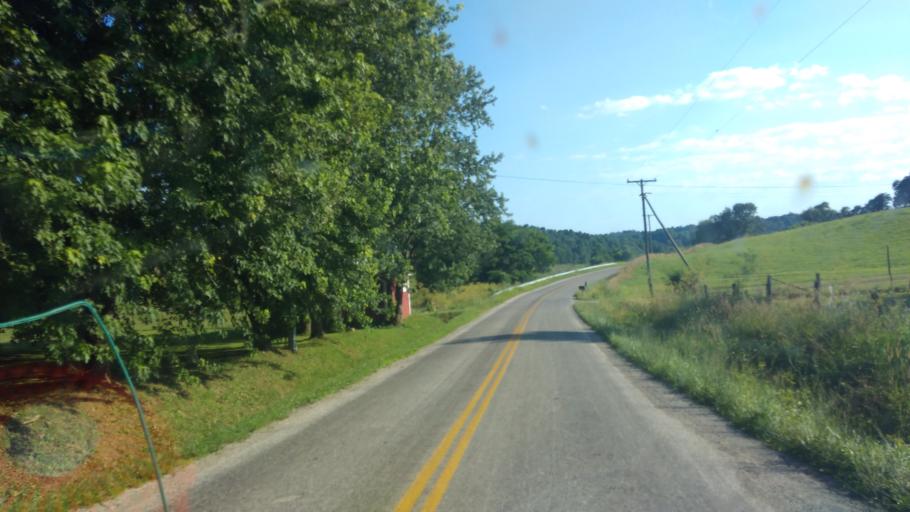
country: US
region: Ohio
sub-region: Ashland County
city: Loudonville
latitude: 40.6916
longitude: -82.2068
